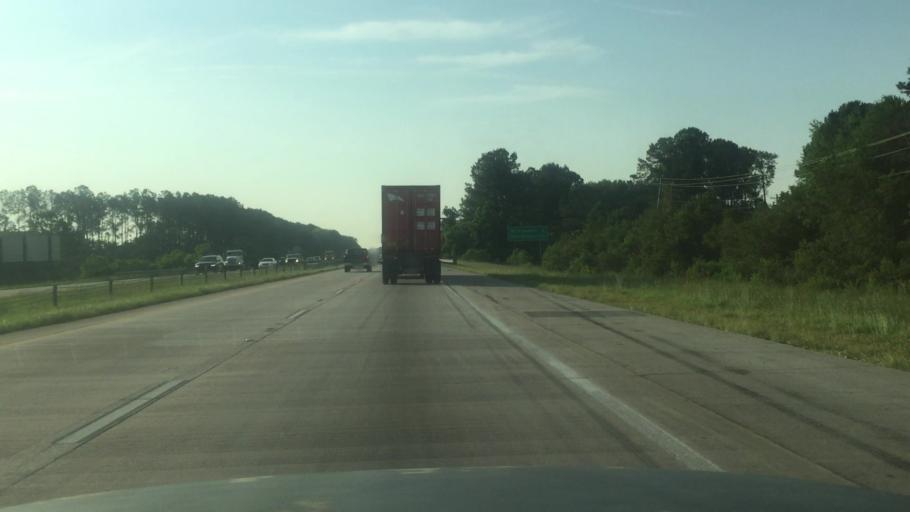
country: US
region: South Carolina
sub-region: Charleston County
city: Mount Pleasant
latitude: 32.8515
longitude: -79.8835
